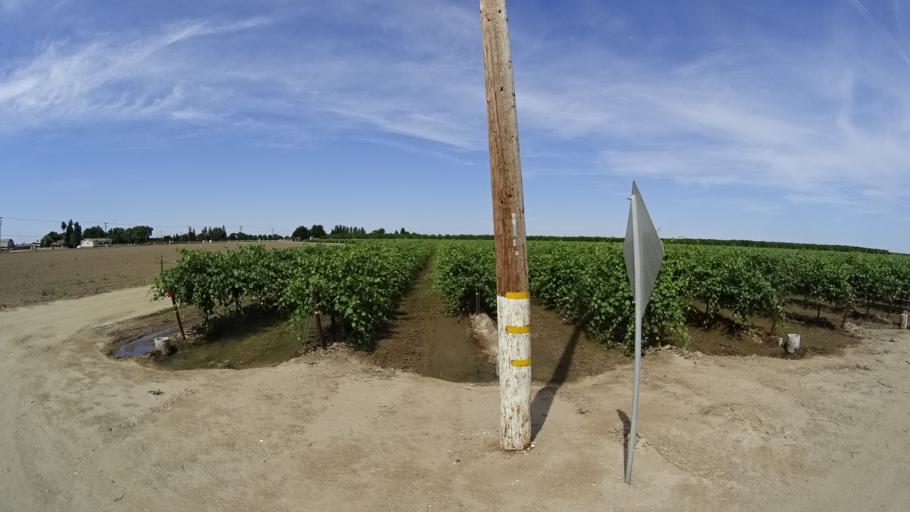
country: US
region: California
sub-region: Kings County
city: Hanford
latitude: 36.3586
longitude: -119.5920
